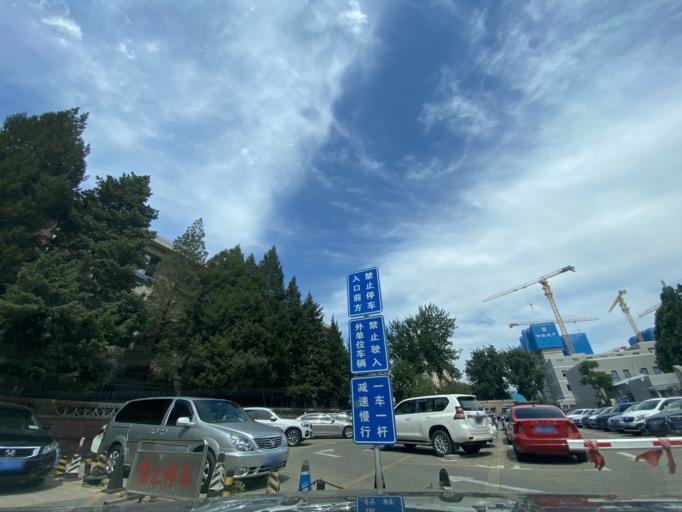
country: CN
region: Beijing
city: Lugu
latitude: 39.9046
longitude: 116.1821
